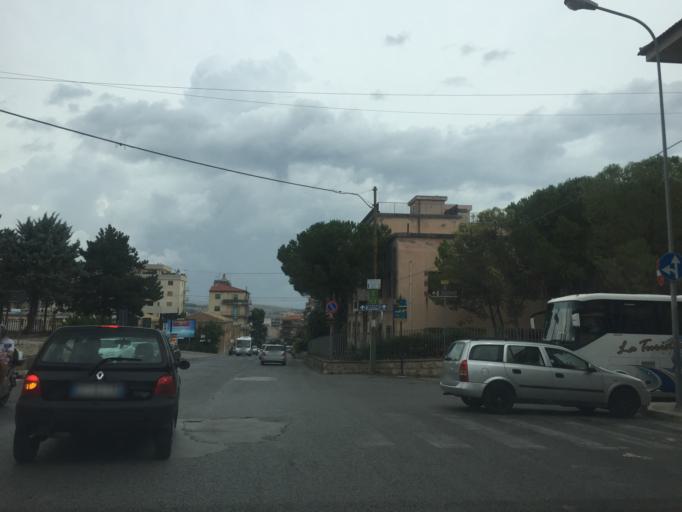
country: IT
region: Sicily
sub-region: Ragusa
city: Ragusa
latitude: 36.9119
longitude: 14.7239
